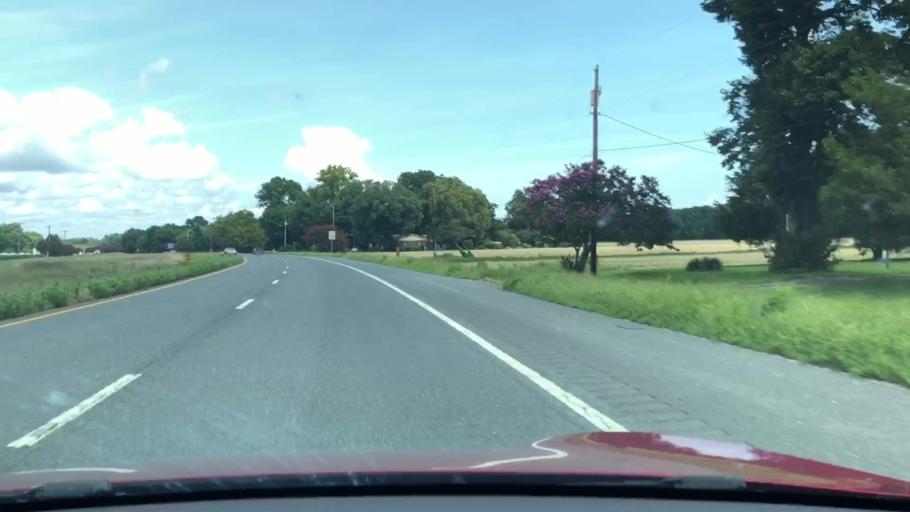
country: US
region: Virginia
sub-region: Northampton County
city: Cape Charles
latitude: 37.2954
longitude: -75.9714
